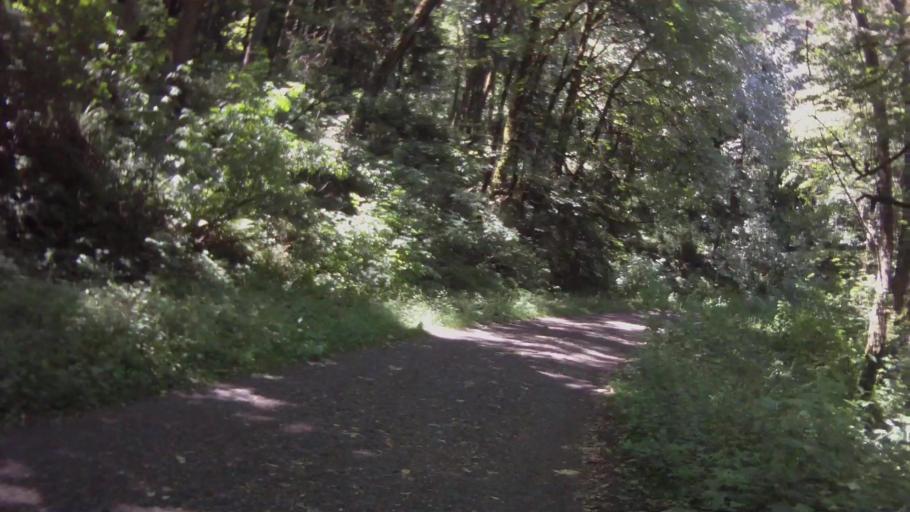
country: US
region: Oregon
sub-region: Washington County
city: West Haven
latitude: 45.5553
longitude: -122.7409
